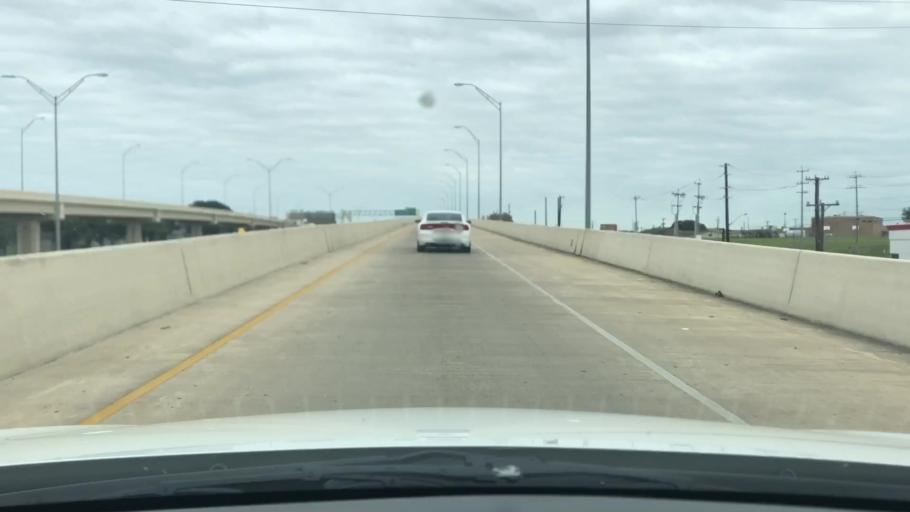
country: US
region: Texas
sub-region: Bexar County
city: Leon Valley
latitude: 29.4845
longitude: -98.5936
